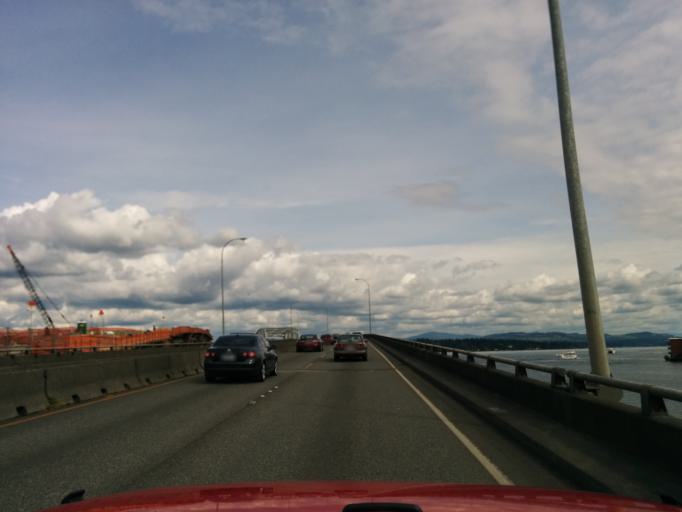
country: US
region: Washington
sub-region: King County
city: Medina
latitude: 47.6437
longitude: -122.2786
